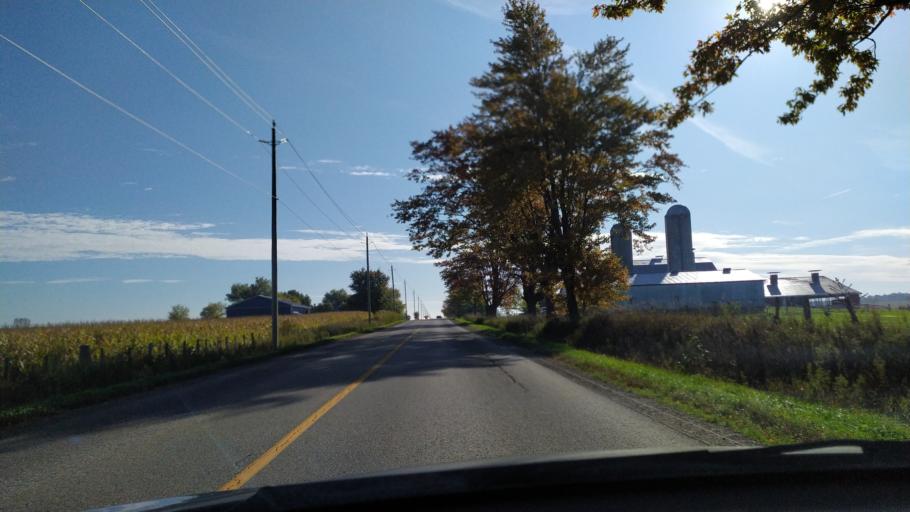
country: CA
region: Ontario
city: Waterloo
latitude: 43.4927
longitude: -80.7281
